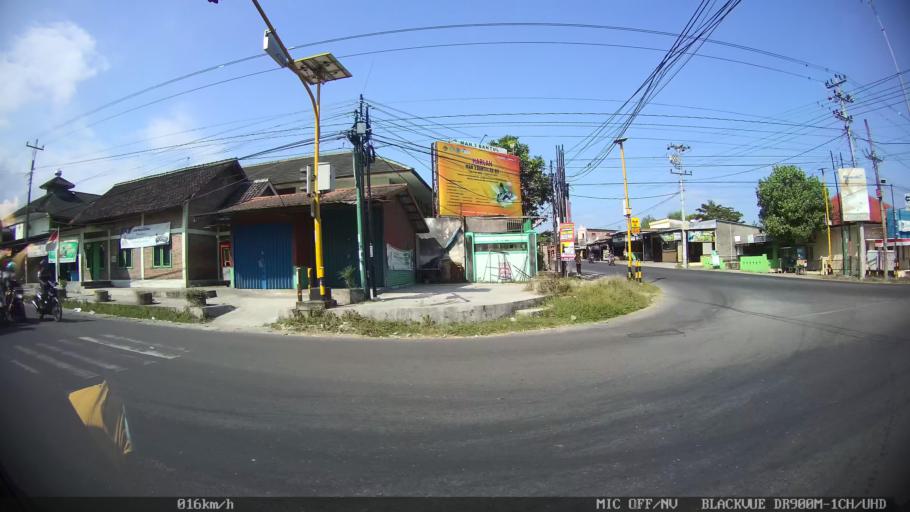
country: ID
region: Daerah Istimewa Yogyakarta
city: Sewon
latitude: -7.8700
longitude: 110.3909
